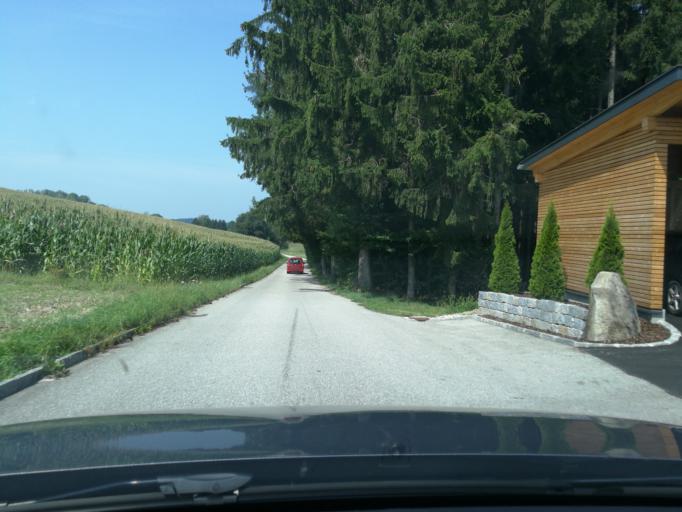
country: DE
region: Bavaria
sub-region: Lower Bavaria
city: Obernzell
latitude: 48.3682
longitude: 13.6636
